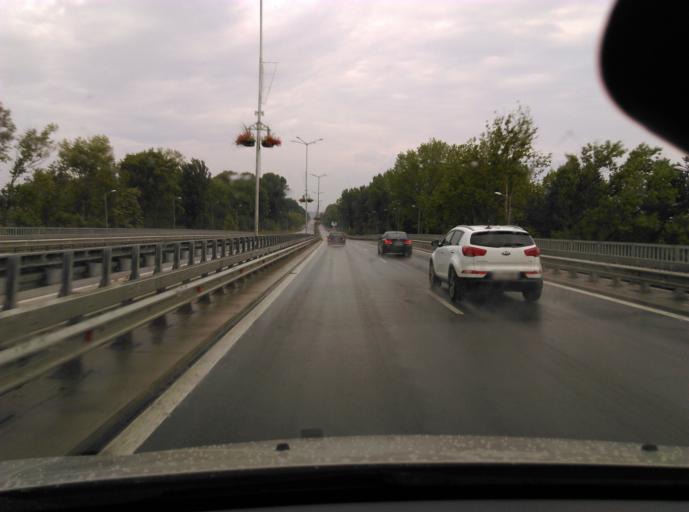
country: BG
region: Burgas
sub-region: Obshtina Burgas
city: Burgas
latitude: 42.4727
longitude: 27.4358
